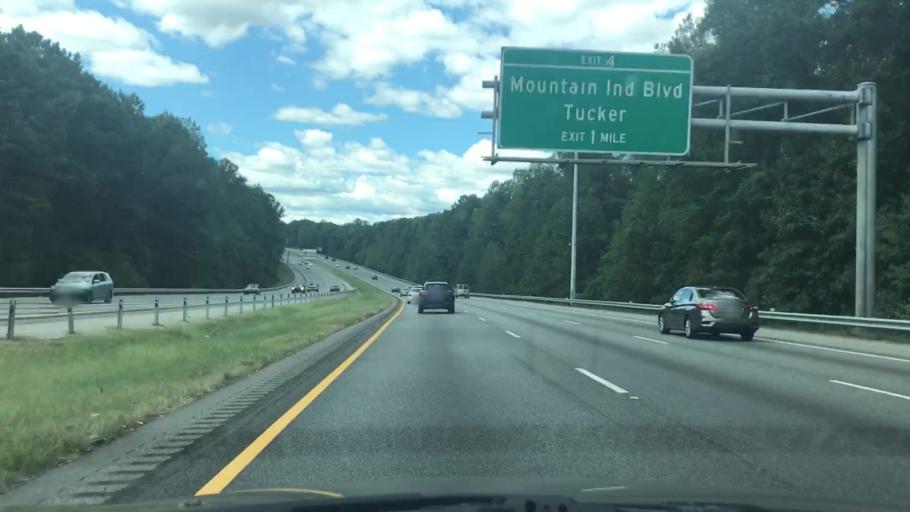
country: US
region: Georgia
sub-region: DeKalb County
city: Stone Mountain
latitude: 33.8300
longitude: -84.1801
